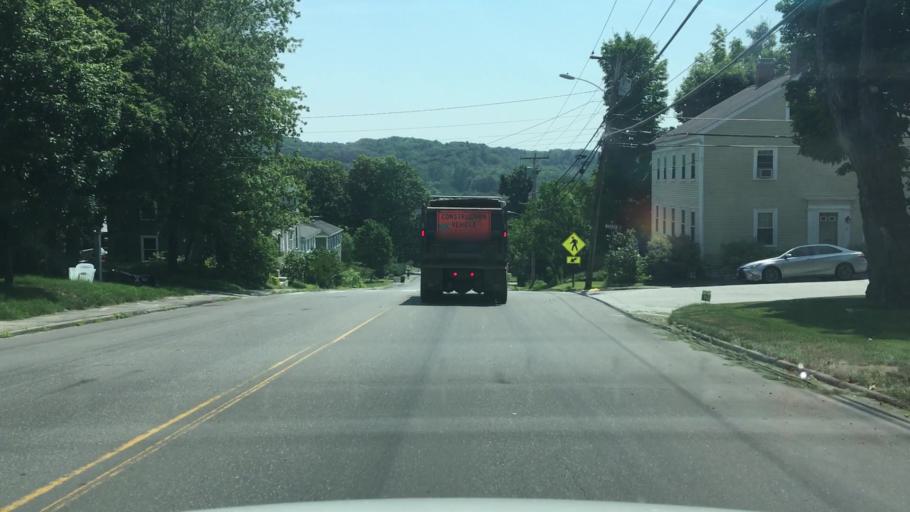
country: US
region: Maine
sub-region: Kennebec County
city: Hallowell
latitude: 44.2888
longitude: -69.7947
